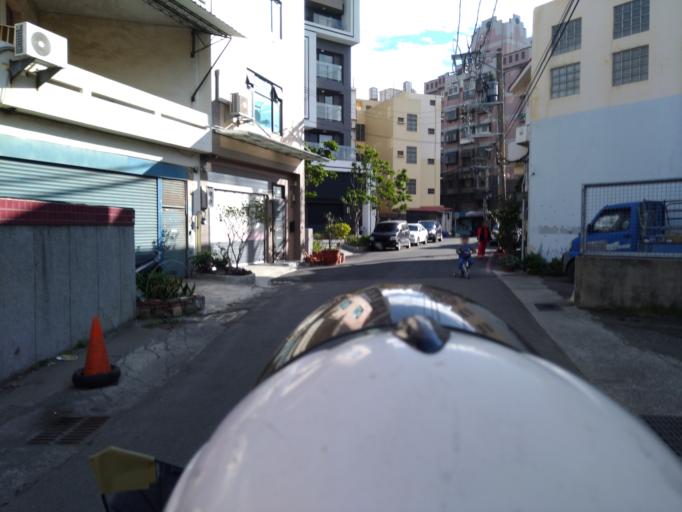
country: TW
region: Taiwan
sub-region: Hsinchu
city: Hsinchu
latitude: 24.8235
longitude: 120.9764
